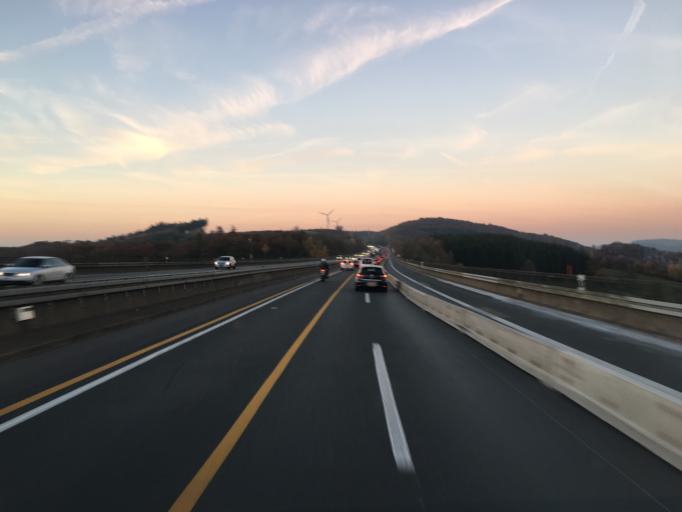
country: DE
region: North Rhine-Westphalia
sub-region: Regierungsbezirk Arnsberg
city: Nachrodt-Wiblingwerde
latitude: 51.2986
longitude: 7.5532
